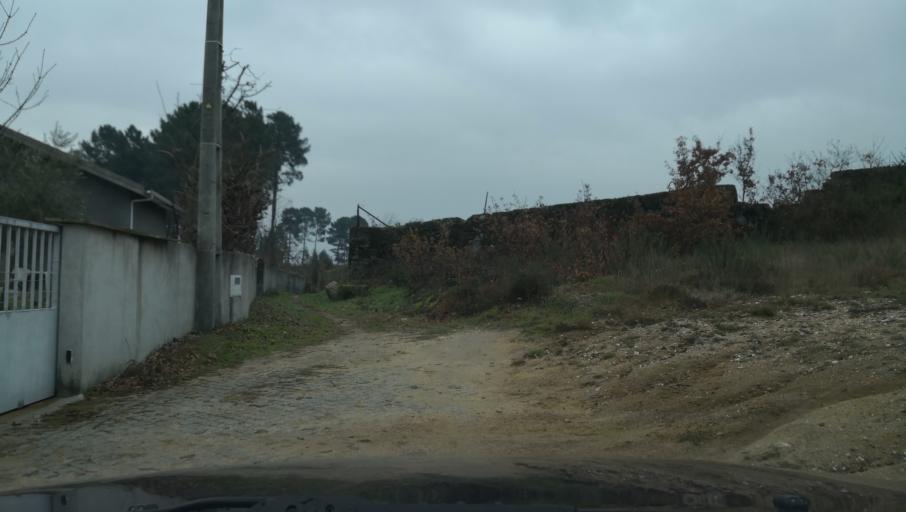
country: PT
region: Vila Real
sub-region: Vila Real
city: Vila Real
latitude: 41.3007
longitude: -7.7735
